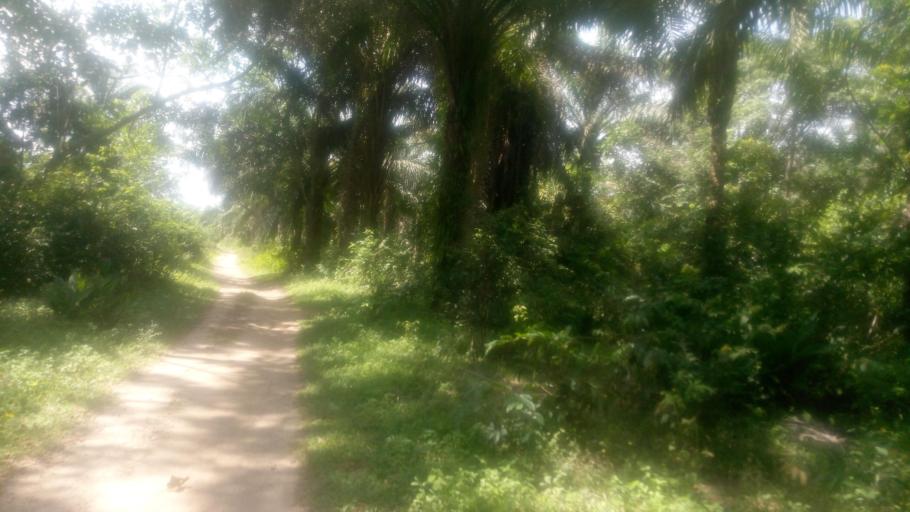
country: SL
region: Northern Province
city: Magburaka
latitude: 8.6524
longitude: -12.0693
